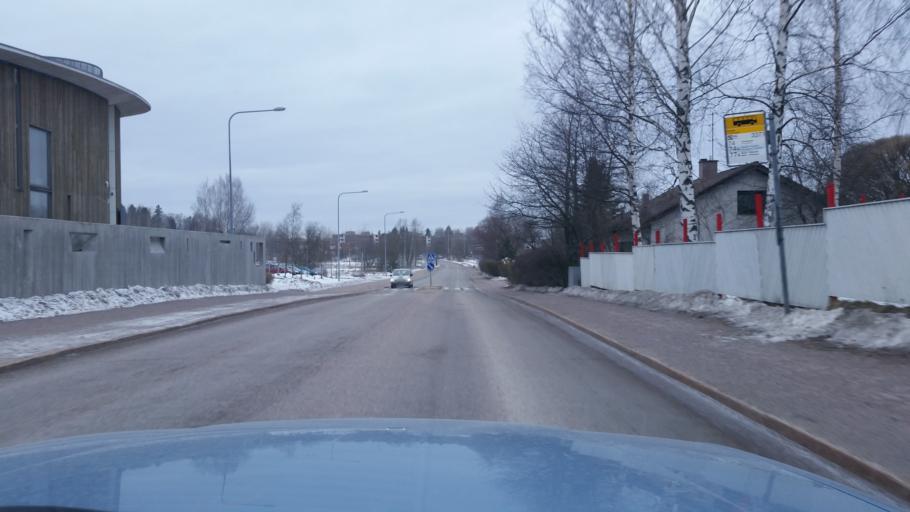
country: FI
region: Uusimaa
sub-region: Helsinki
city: Vantaa
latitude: 60.2493
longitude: 25.0321
